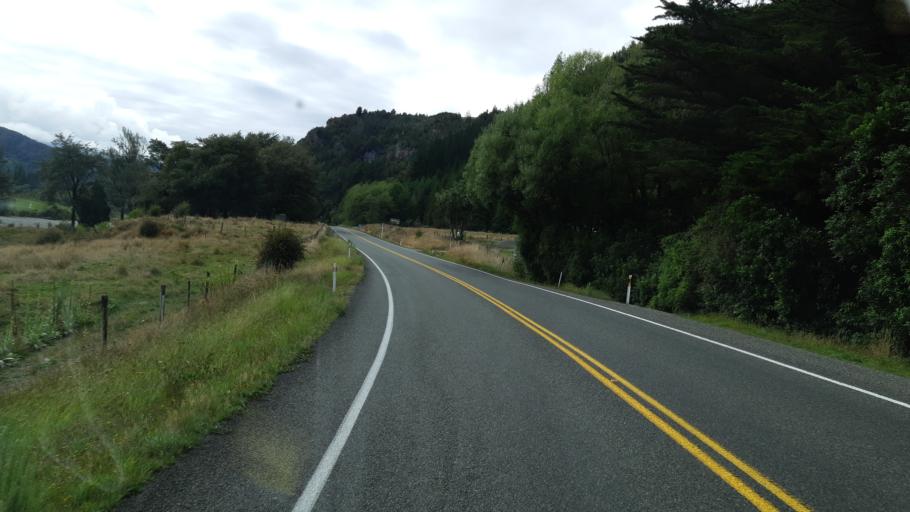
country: NZ
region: West Coast
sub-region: Buller District
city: Westport
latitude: -41.7813
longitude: 172.2612
